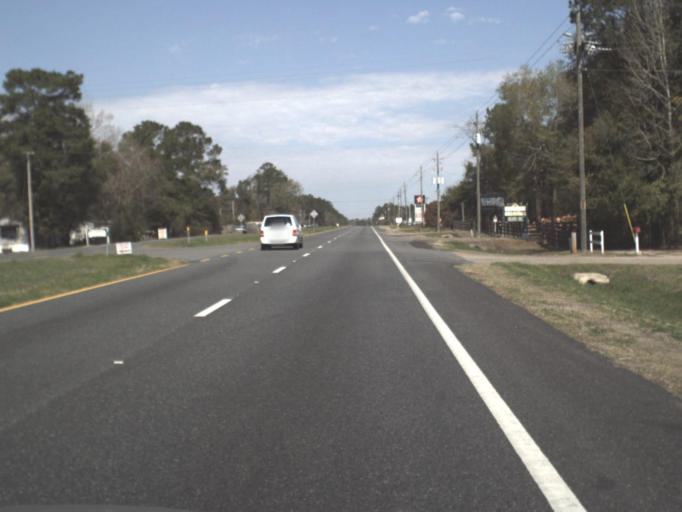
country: US
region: Florida
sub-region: Gadsden County
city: Havana
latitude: 30.5722
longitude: -84.3949
